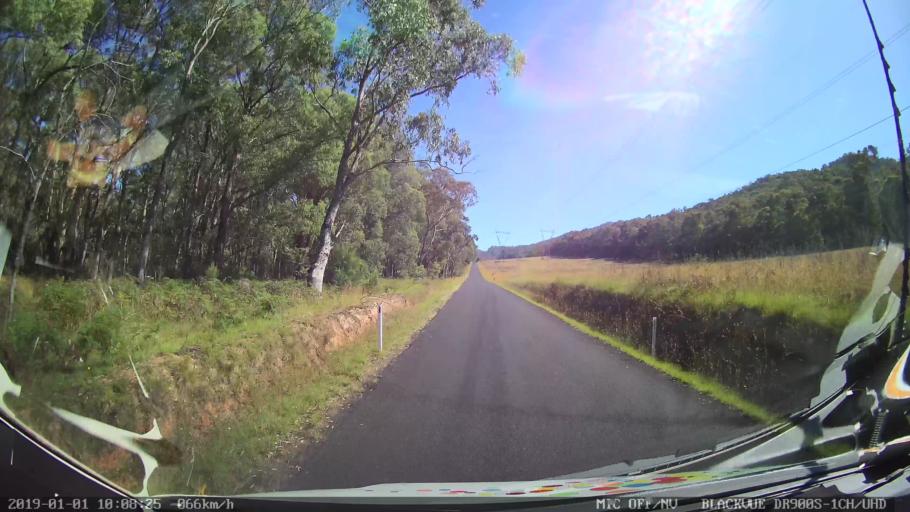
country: AU
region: New South Wales
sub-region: Snowy River
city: Jindabyne
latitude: -36.1596
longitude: 148.1575
